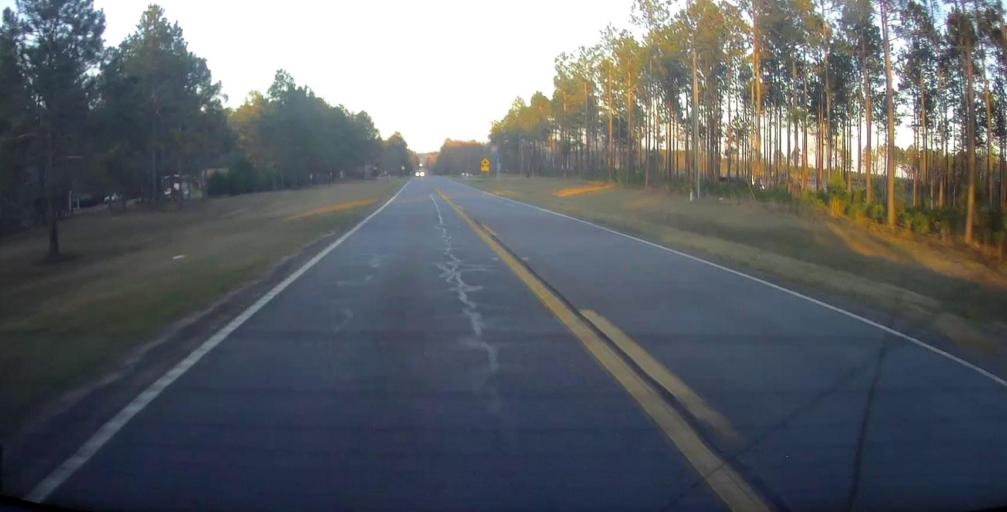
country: US
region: Georgia
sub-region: Dodge County
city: Eastman
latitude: 32.2809
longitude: -83.1072
